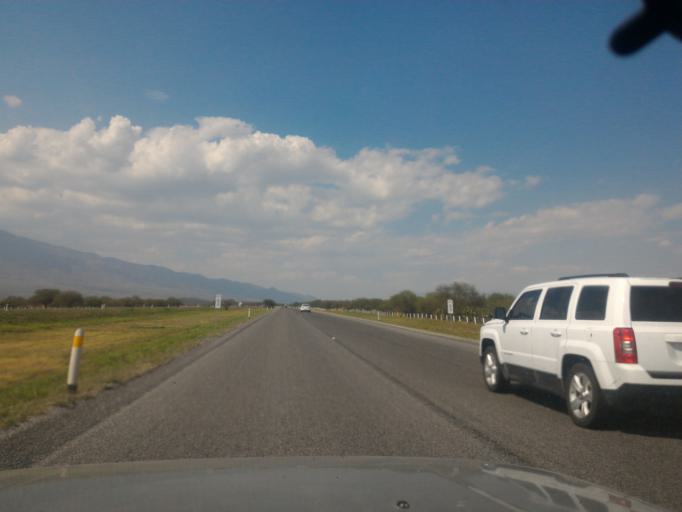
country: MX
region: Jalisco
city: Atoyac
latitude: 19.9802
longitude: -103.5359
